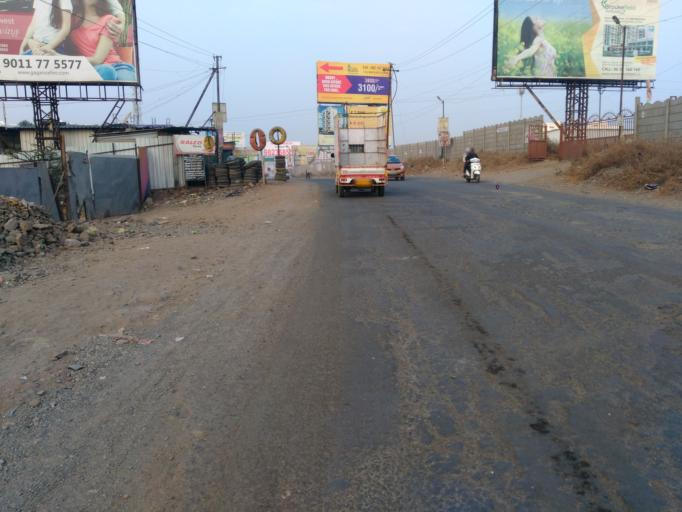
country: IN
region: Maharashtra
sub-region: Pune Division
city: Pune
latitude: 18.4501
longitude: 73.9119
